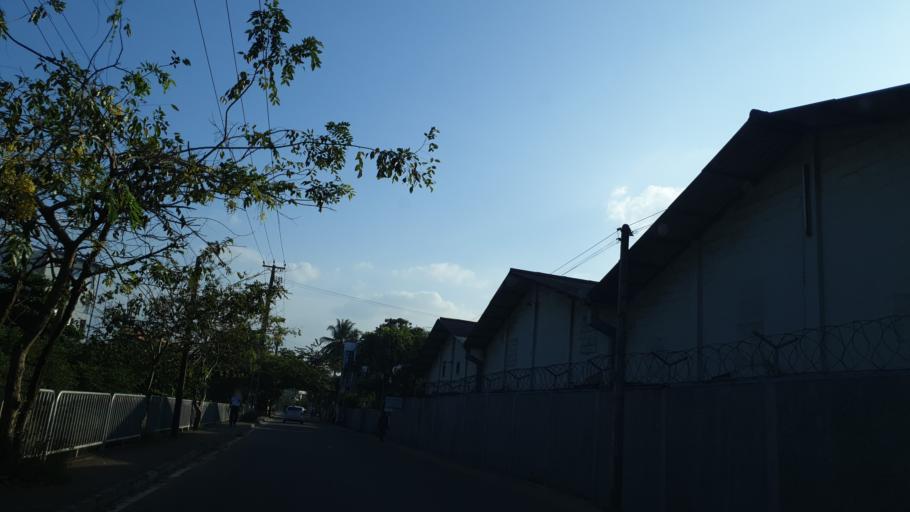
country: LK
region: Western
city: Galkissa
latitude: 6.8476
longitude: 79.8771
